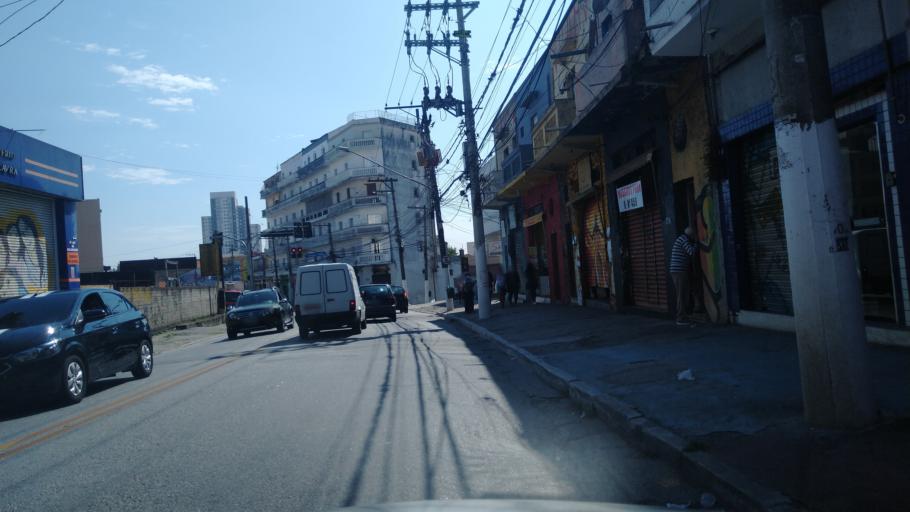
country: BR
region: Sao Paulo
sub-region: Guarulhos
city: Guarulhos
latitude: -23.4804
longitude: -46.6003
